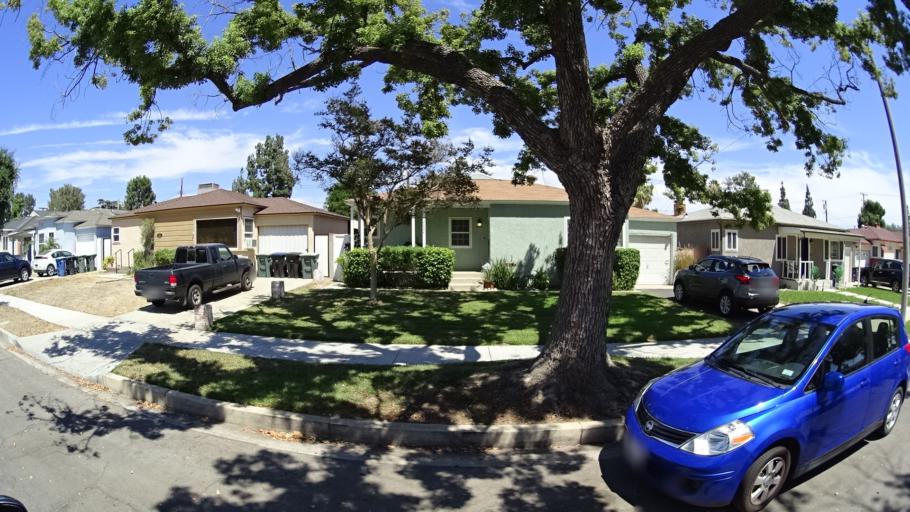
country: US
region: California
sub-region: Los Angeles County
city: North Hollywood
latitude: 34.1860
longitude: -118.3555
